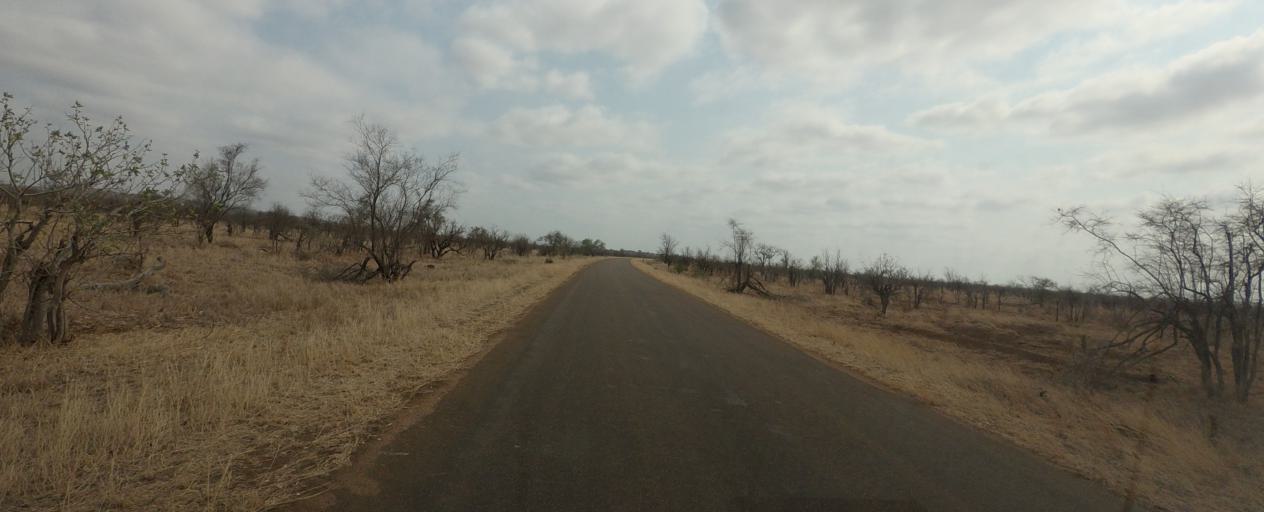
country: ZA
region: Limpopo
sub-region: Vhembe District Municipality
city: Mutale
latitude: -22.6120
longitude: 31.1737
